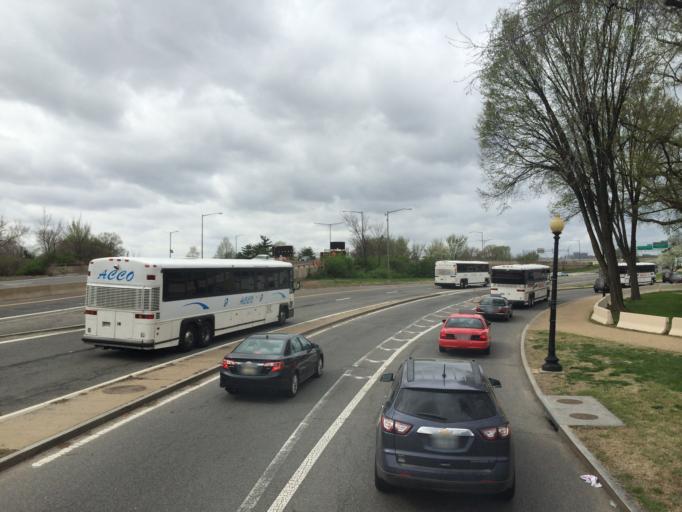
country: US
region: Washington, D.C.
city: Washington, D.C.
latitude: 38.8802
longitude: -77.0349
